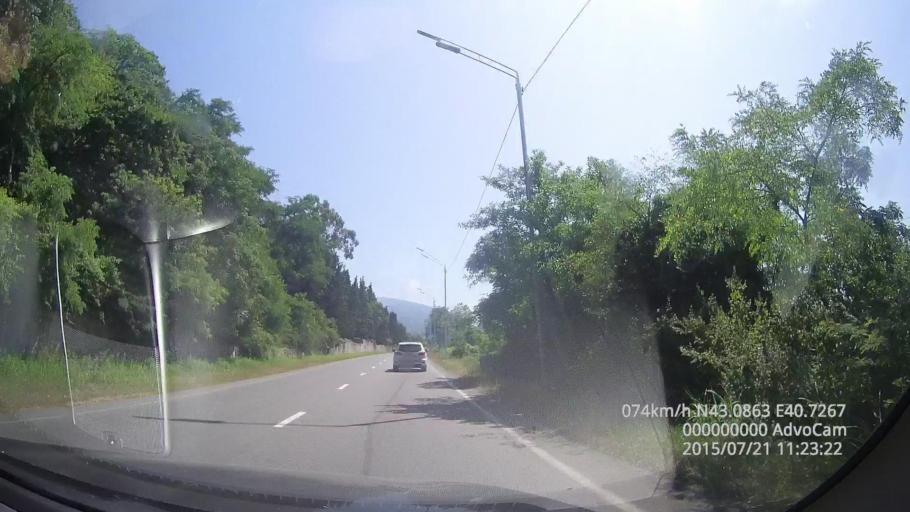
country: GE
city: P'rimorsk'oe
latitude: 43.0863
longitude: 40.7271
